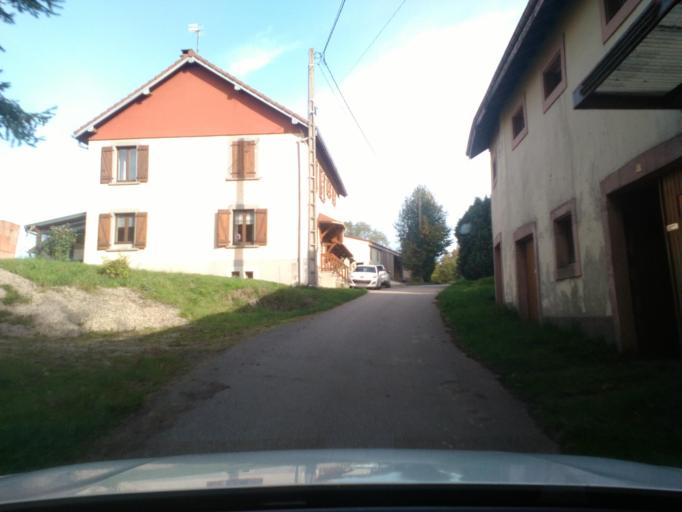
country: FR
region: Lorraine
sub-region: Departement des Vosges
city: Senones
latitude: 48.3539
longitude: 7.0230
